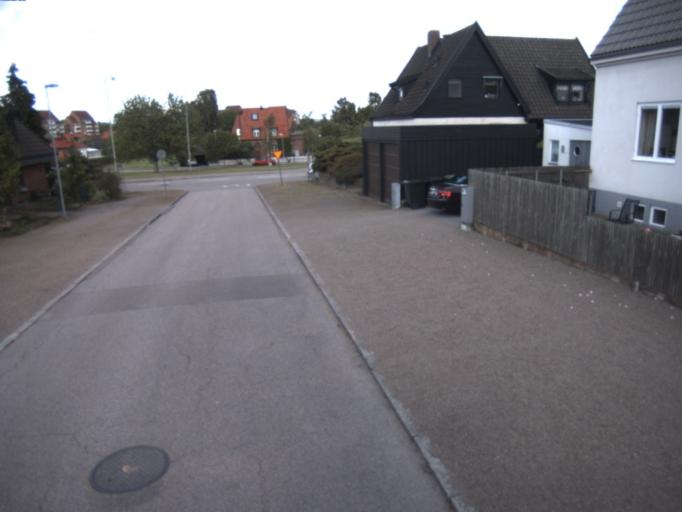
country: SE
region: Skane
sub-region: Helsingborg
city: Helsingborg
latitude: 56.0492
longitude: 12.7153
